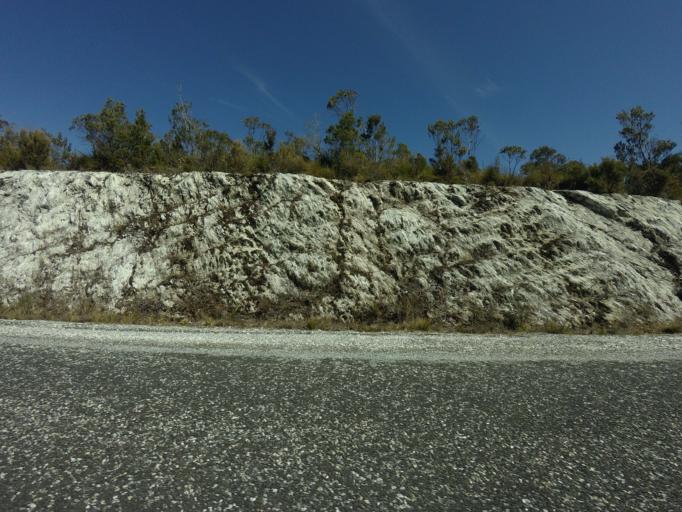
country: AU
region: Tasmania
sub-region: Huon Valley
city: Geeveston
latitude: -42.8364
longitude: 146.1296
